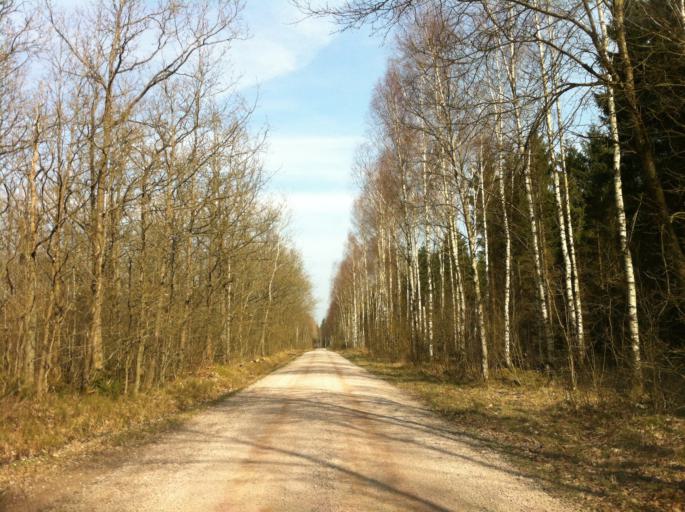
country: SE
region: Skane
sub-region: Eslovs Kommun
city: Stehag
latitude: 56.0013
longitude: 13.3290
